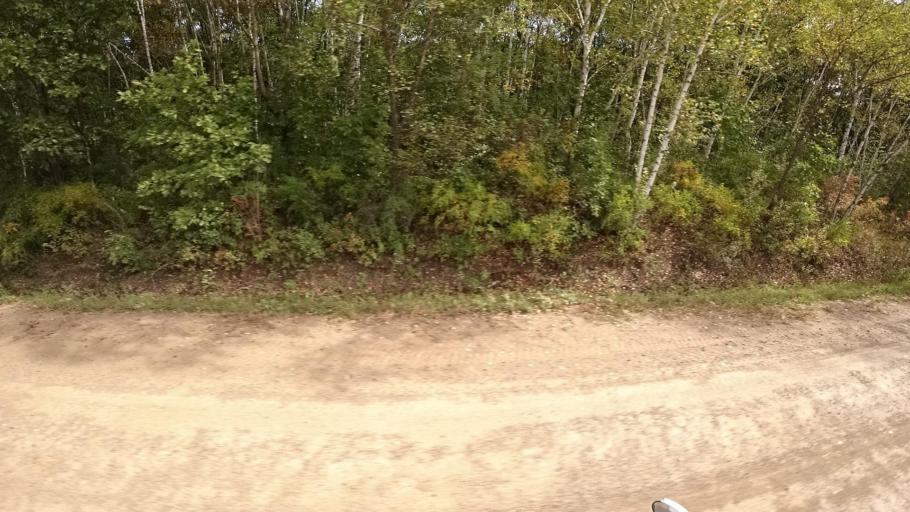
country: RU
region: Primorskiy
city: Yakovlevka
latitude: 44.7370
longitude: 133.6079
